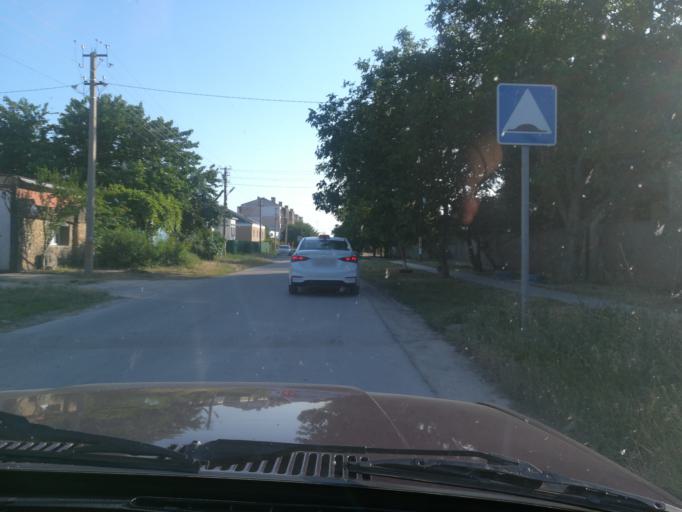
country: RU
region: Krasnodarskiy
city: Vityazevo
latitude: 45.0057
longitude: 37.2911
